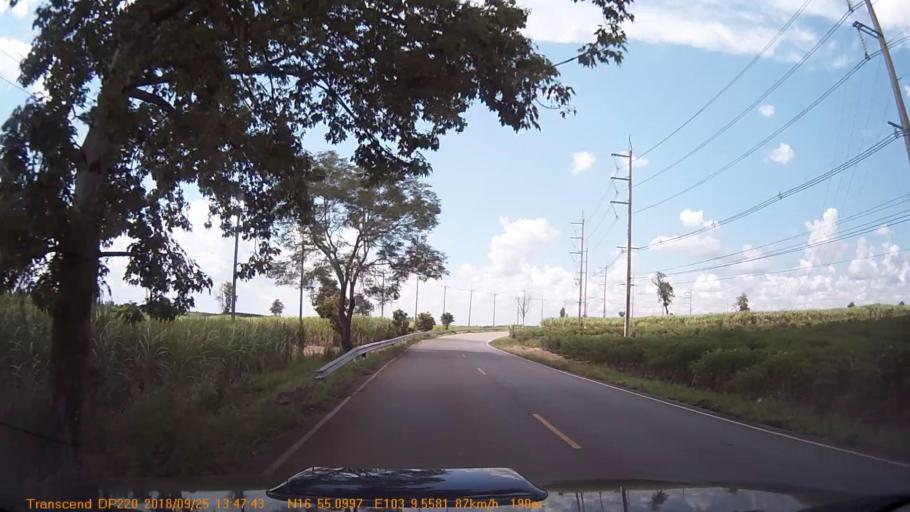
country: TH
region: Changwat Udon Thani
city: Si That
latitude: 16.9184
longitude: 103.1593
